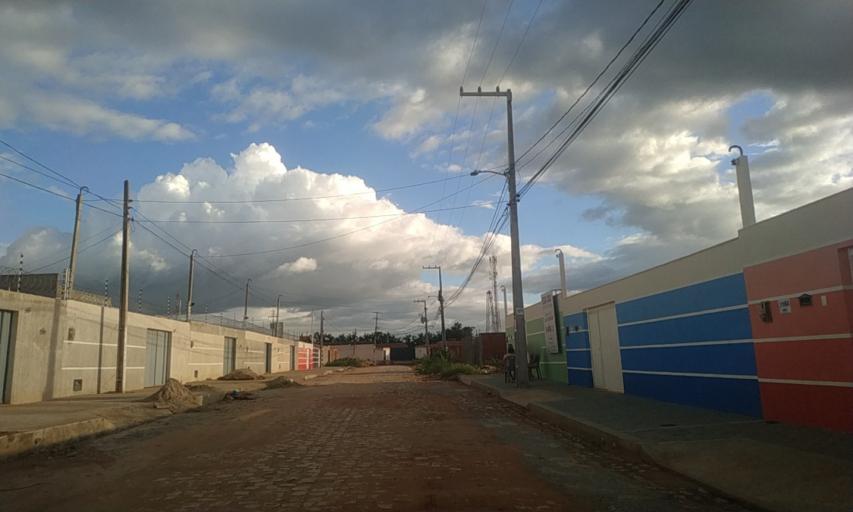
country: BR
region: Rio Grande do Norte
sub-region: Mossoro
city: Mossoro
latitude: -5.2229
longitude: -37.3423
